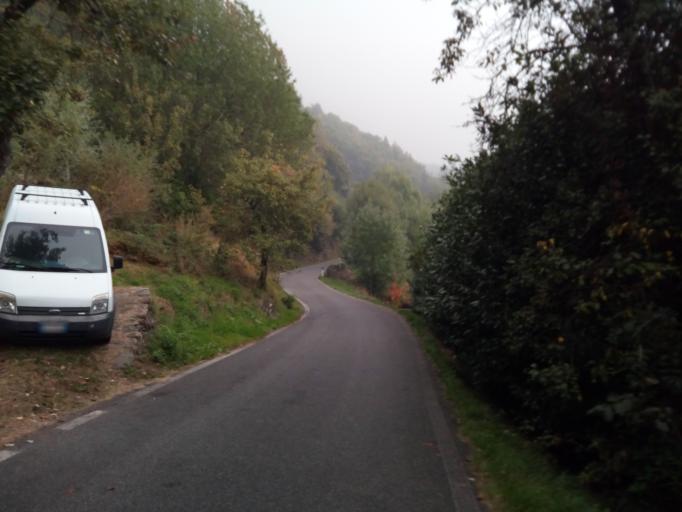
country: IT
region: Piedmont
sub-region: Provincia di Torino
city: Settimo Vittone
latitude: 45.5502
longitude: 7.8463
